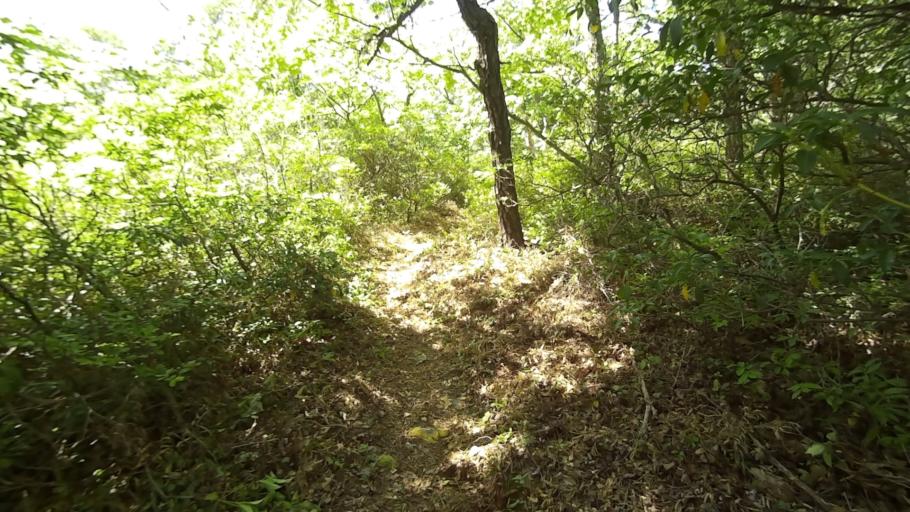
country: US
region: Pennsylvania
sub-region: Centre County
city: Boalsburg
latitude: 40.7215
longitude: -77.7838
